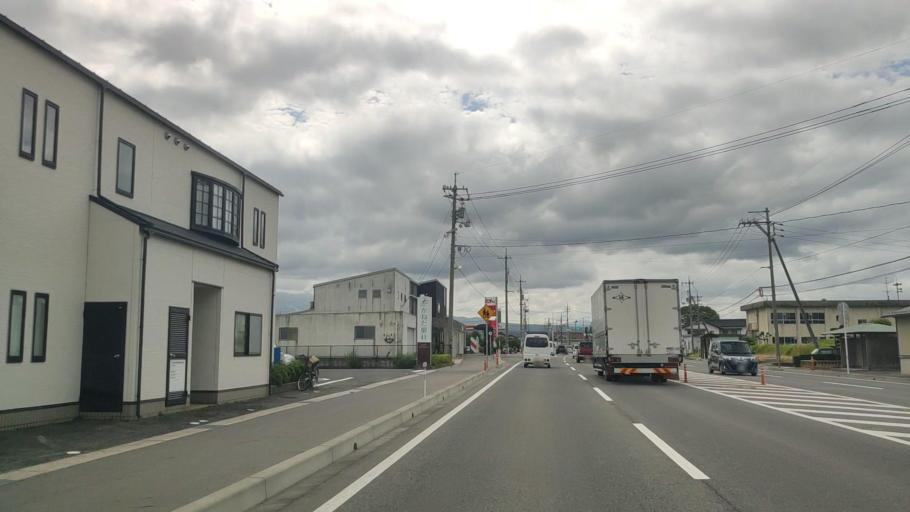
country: JP
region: Tottori
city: Yonago
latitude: 35.3989
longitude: 133.3776
